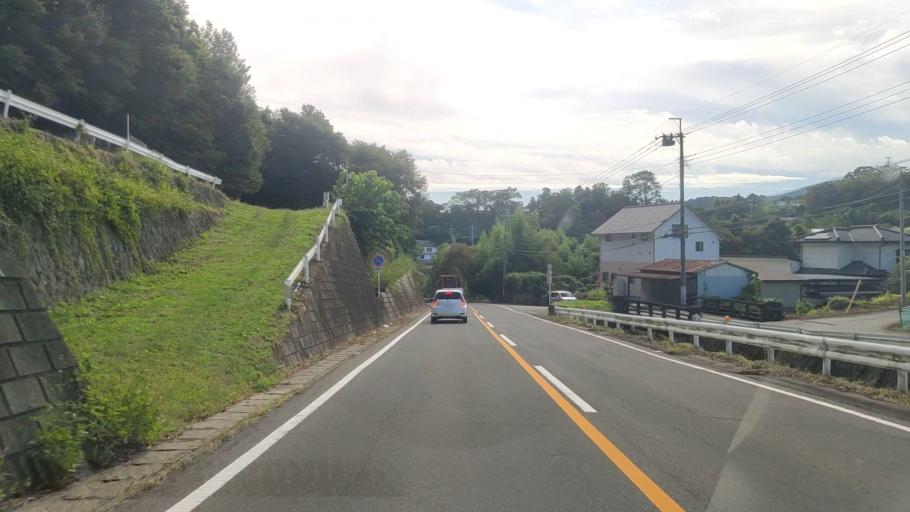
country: JP
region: Gunma
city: Numata
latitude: 36.6249
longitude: 139.0221
